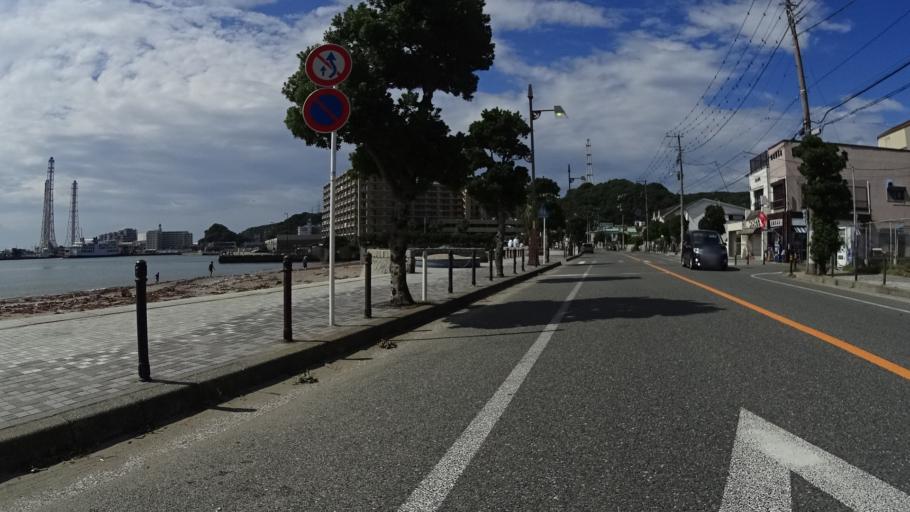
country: JP
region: Kanagawa
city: Yokosuka
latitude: 35.2252
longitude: 139.7134
